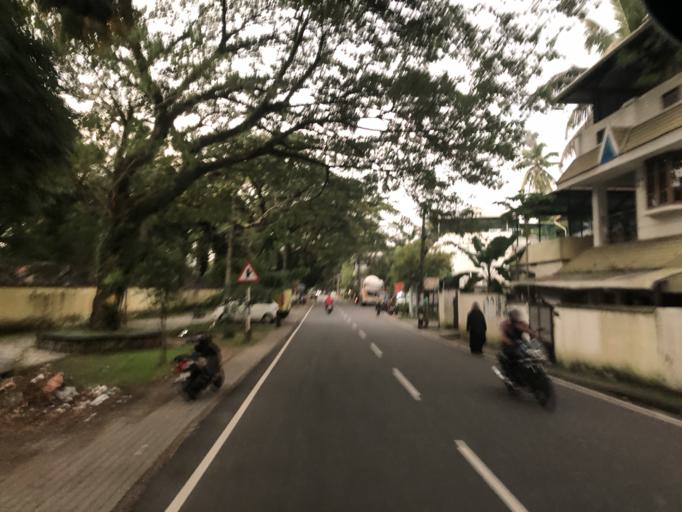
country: IN
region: Kerala
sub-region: Ernakulam
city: Cochin
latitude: 9.9543
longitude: 76.2410
